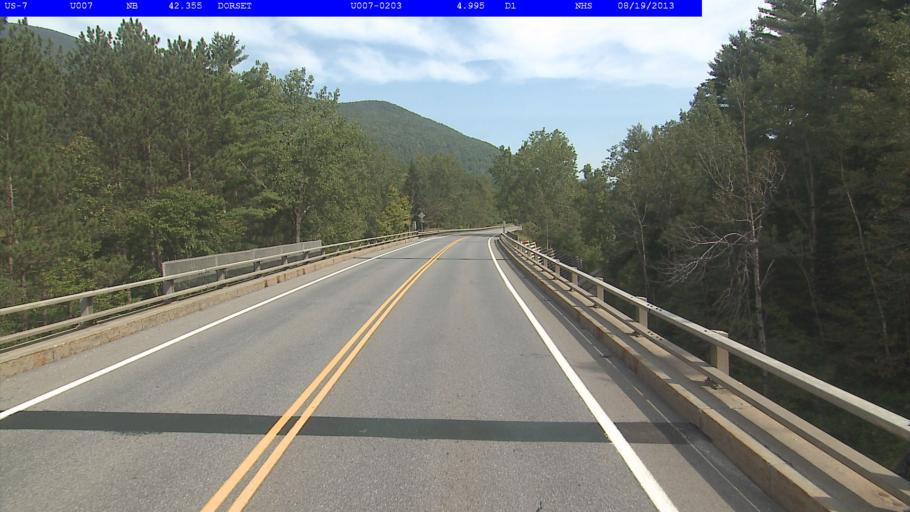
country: US
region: Vermont
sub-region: Bennington County
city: Manchester Center
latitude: 43.2807
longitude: -73.0030
